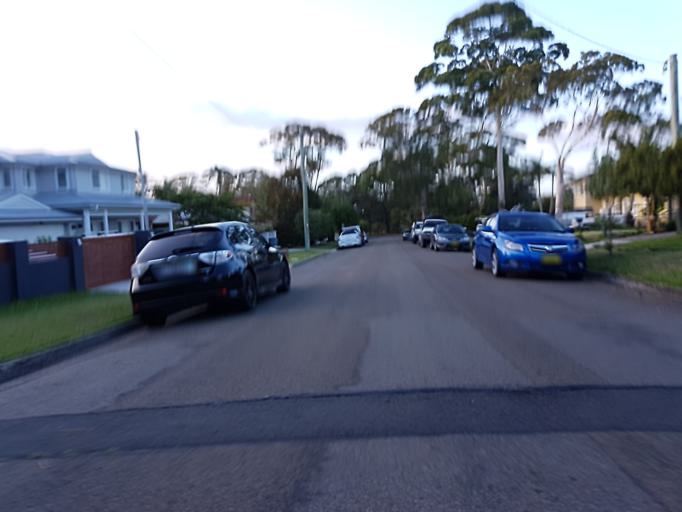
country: AU
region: New South Wales
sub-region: Warringah
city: Killarney Heights
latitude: -33.7577
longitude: 151.2294
